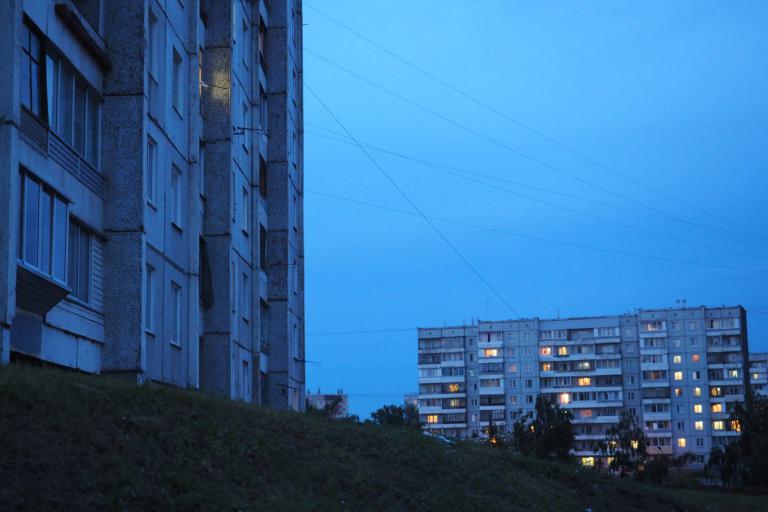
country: RU
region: Krasnoyarskiy
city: Solnechnyy
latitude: 56.1163
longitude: 92.9236
